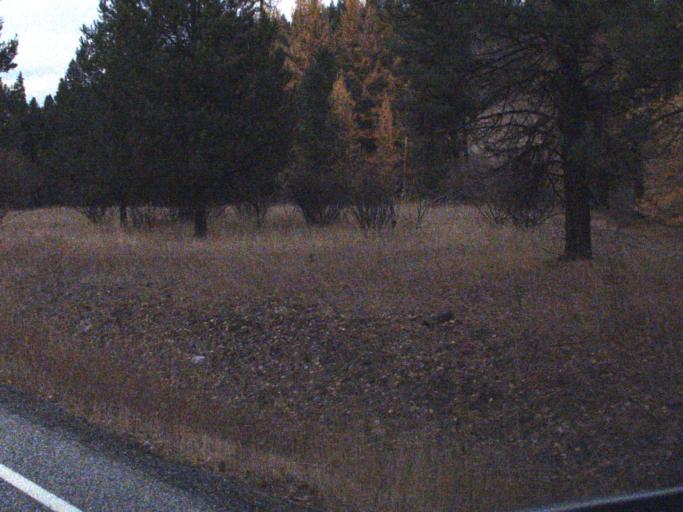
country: US
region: Washington
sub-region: Ferry County
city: Republic
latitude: 48.6095
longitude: -118.6609
